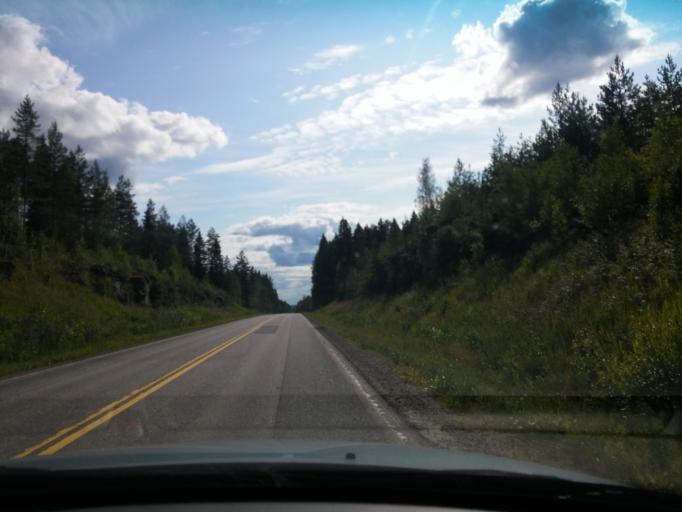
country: FI
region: Central Finland
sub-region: Keuruu
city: Keuruu
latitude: 62.3061
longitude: 24.7264
